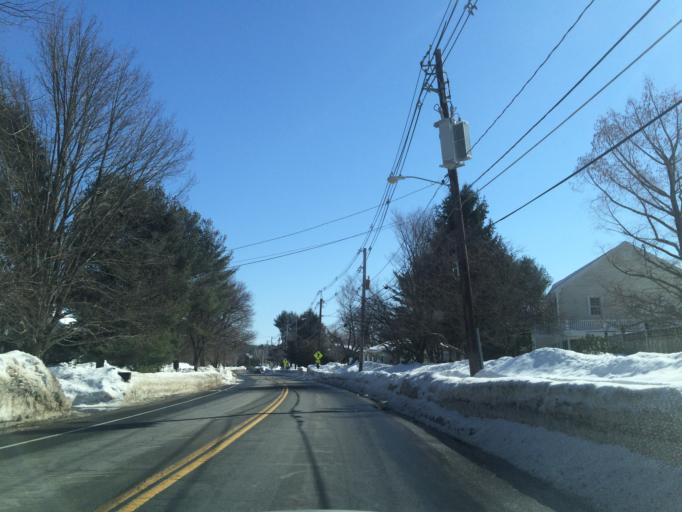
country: US
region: Massachusetts
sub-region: Norfolk County
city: Wellesley
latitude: 42.2898
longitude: -71.2673
